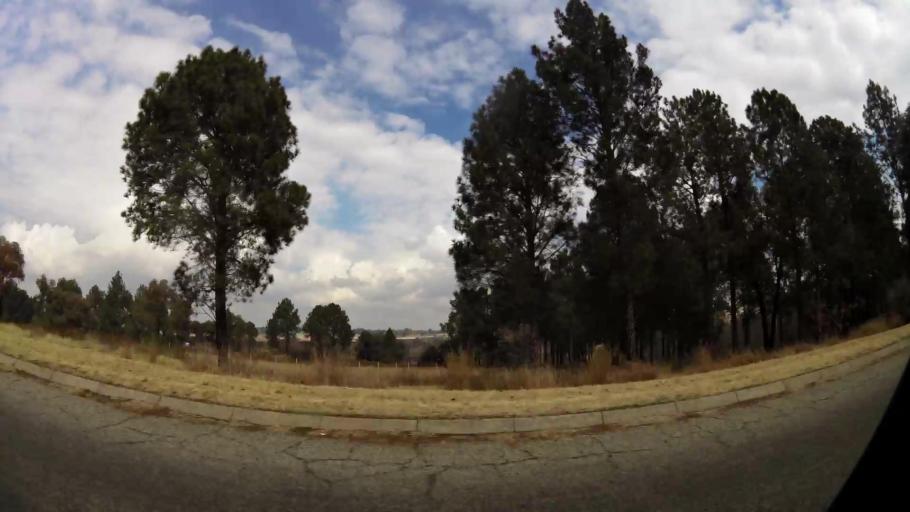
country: ZA
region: Gauteng
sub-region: Sedibeng District Municipality
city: Vanderbijlpark
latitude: -26.7433
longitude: 27.8462
